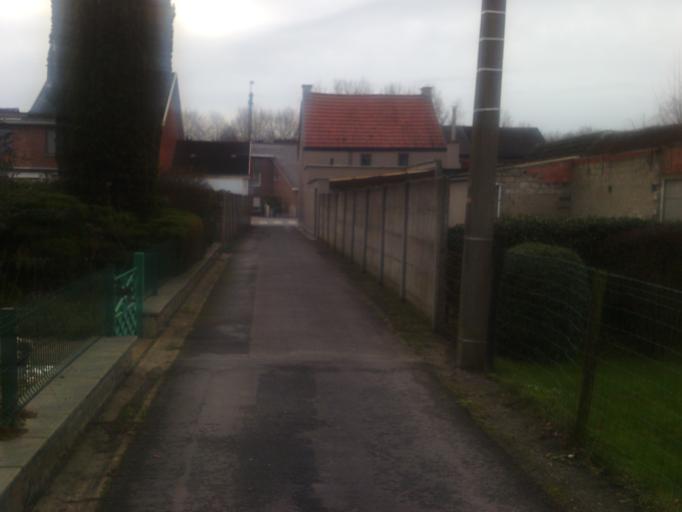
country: BE
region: Flanders
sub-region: Provincie Oost-Vlaanderen
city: Berlare
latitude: 51.0252
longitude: 3.9962
